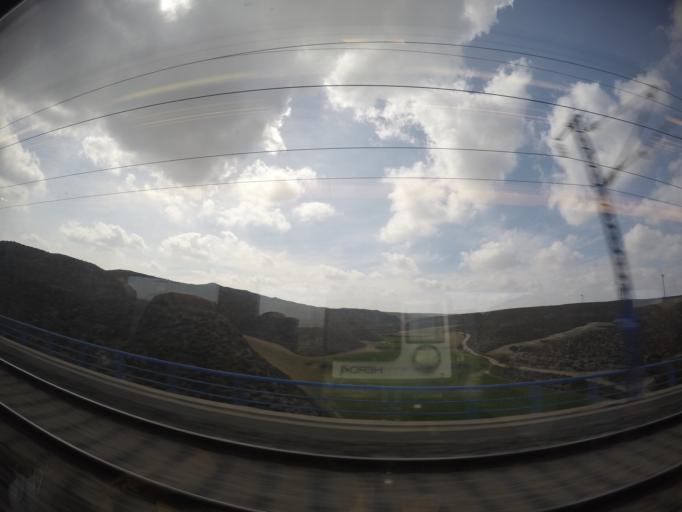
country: ES
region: Aragon
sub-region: Provincia de Zaragoza
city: Fuentes de Ebro
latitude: 41.4980
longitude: -0.6548
